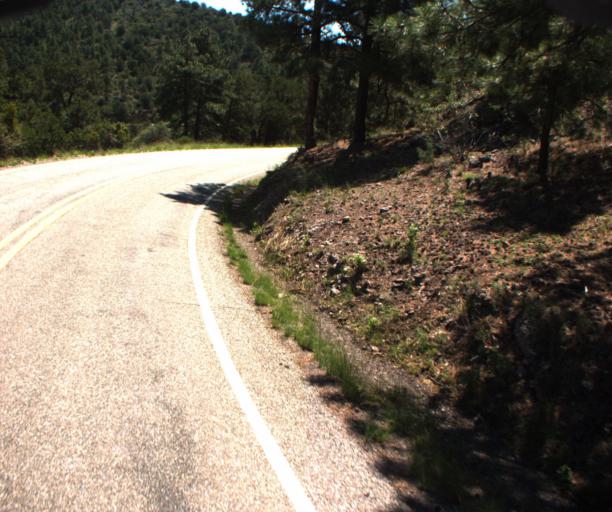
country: US
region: Arizona
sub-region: Greenlee County
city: Morenci
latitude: 33.2397
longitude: -109.3814
